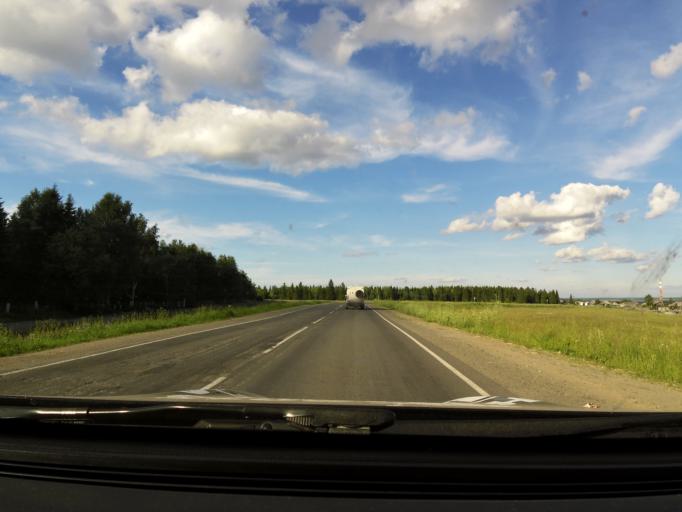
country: RU
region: Kirov
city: Omutninsk
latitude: 58.6923
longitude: 52.1962
